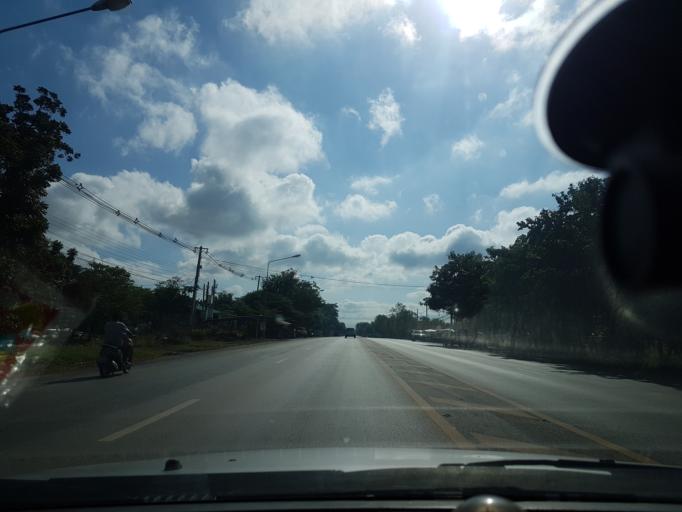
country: TH
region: Lop Buri
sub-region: Amphoe Tha Luang
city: Tha Luang
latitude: 15.0784
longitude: 101.0516
